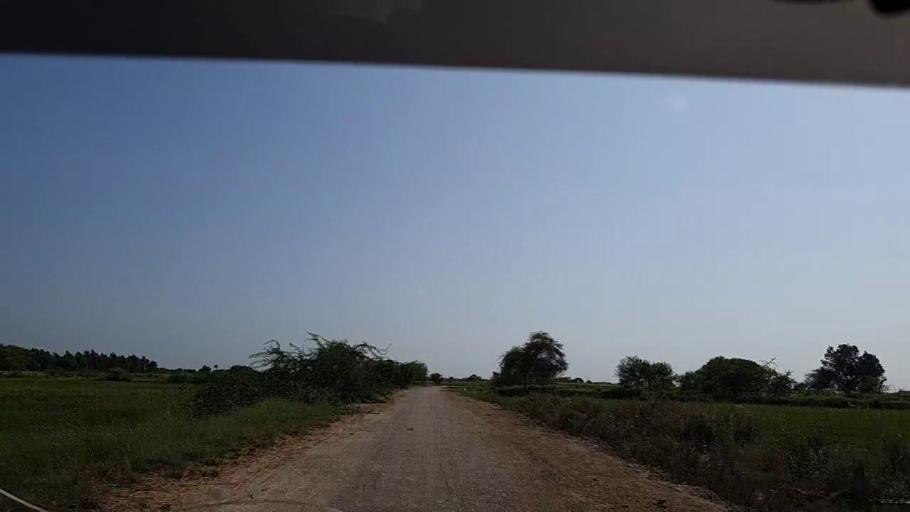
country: PK
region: Sindh
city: Badin
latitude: 24.6247
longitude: 68.7821
